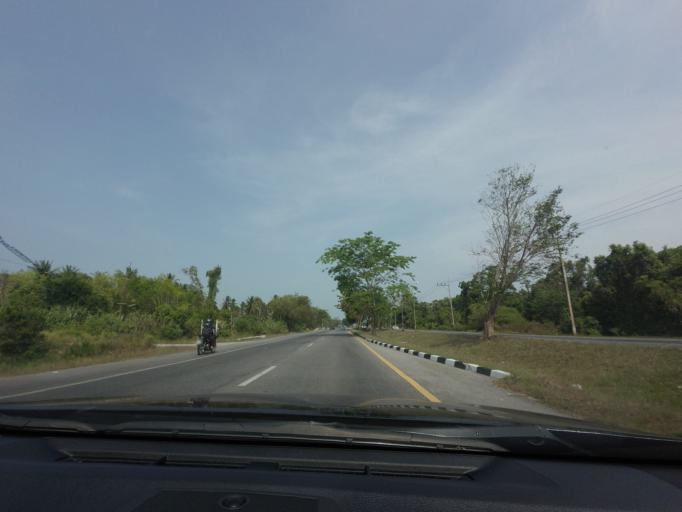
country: TH
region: Pattani
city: Yaring
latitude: 6.8227
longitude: 101.4018
